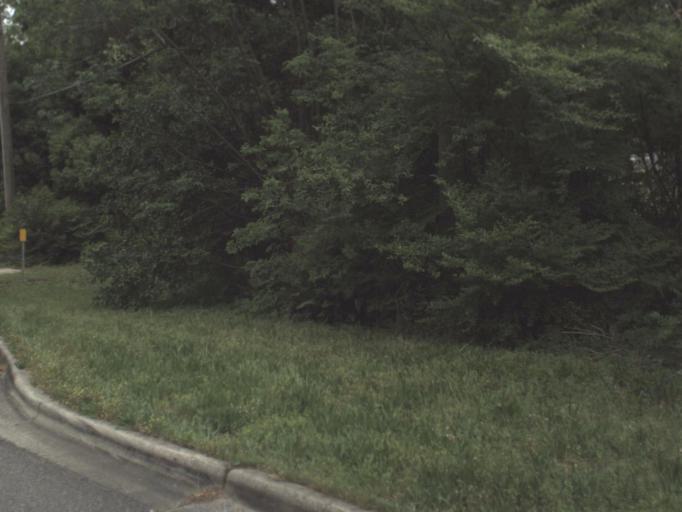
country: US
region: Florida
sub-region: Escambia County
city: Ferry Pass
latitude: 30.4924
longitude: -87.1561
